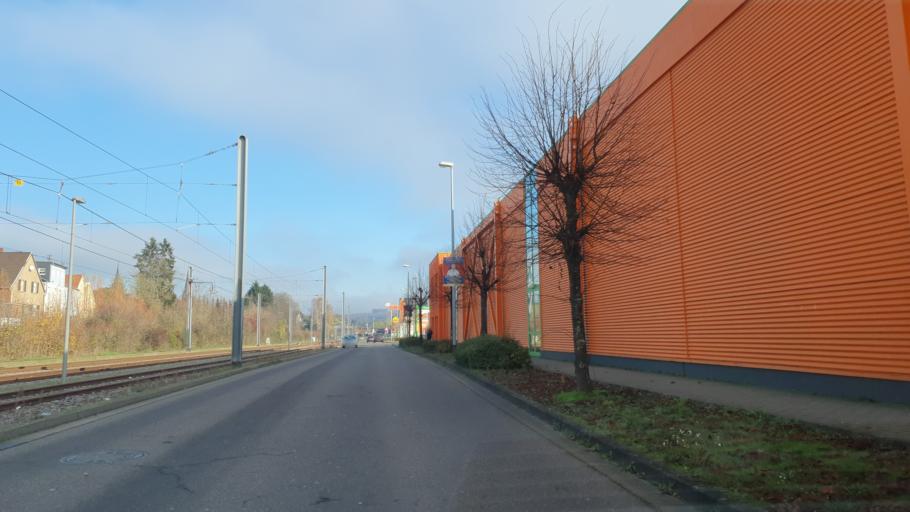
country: DE
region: Saarland
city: Heusweiler
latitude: 49.3340
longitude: 6.9264
